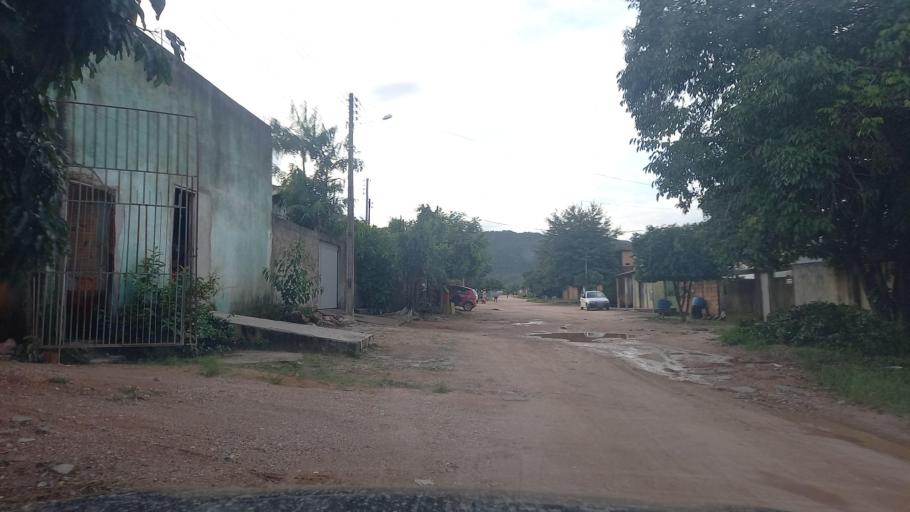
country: BR
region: Goias
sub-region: Cavalcante
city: Cavalcante
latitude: -13.7897
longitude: -47.4560
